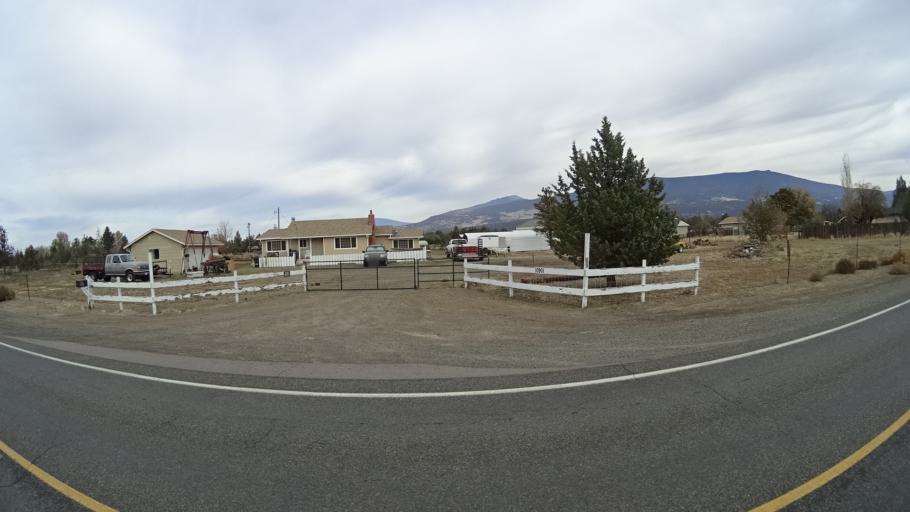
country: US
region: California
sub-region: Siskiyou County
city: Weed
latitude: 41.6027
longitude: -122.3531
